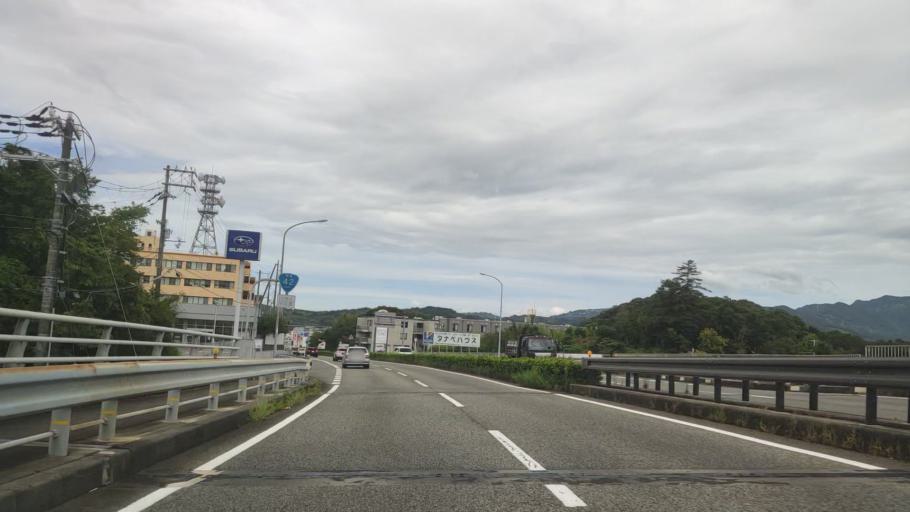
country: JP
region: Wakayama
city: Tanabe
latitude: 33.7353
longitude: 135.4000
